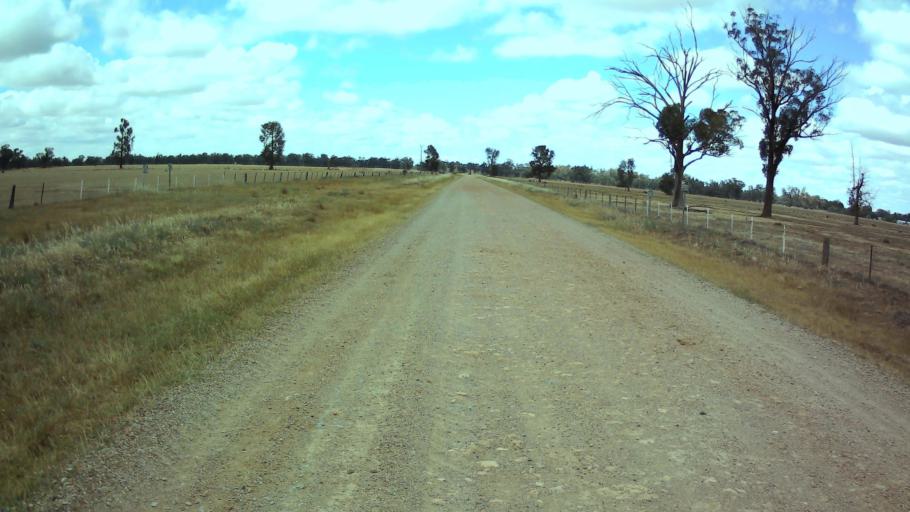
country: AU
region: New South Wales
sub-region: Weddin
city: Grenfell
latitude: -34.0218
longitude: 147.9143
